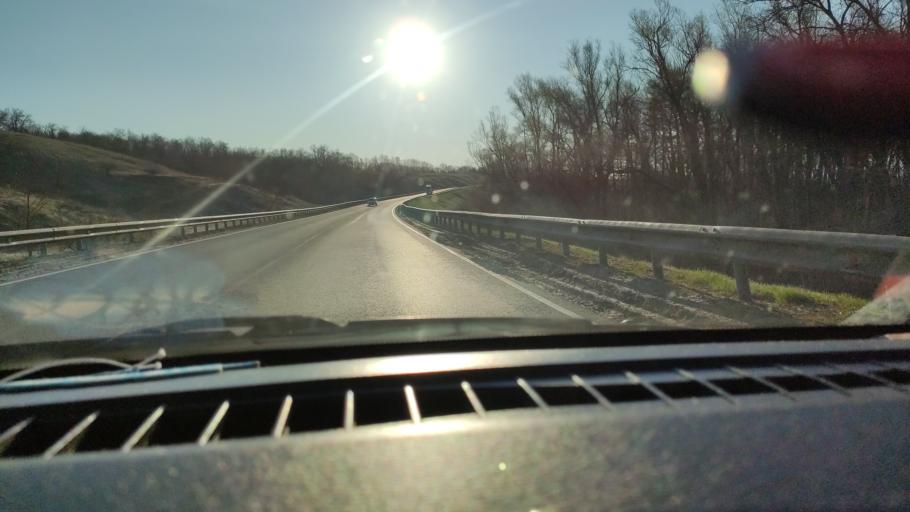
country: RU
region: Saratov
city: Tersa
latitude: 52.1037
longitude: 47.4873
